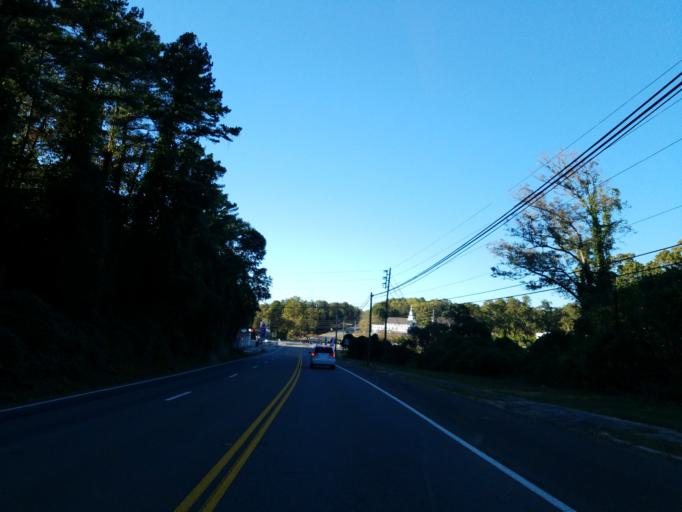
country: US
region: Georgia
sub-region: Pickens County
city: Nelson
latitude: 34.4115
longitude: -84.3875
